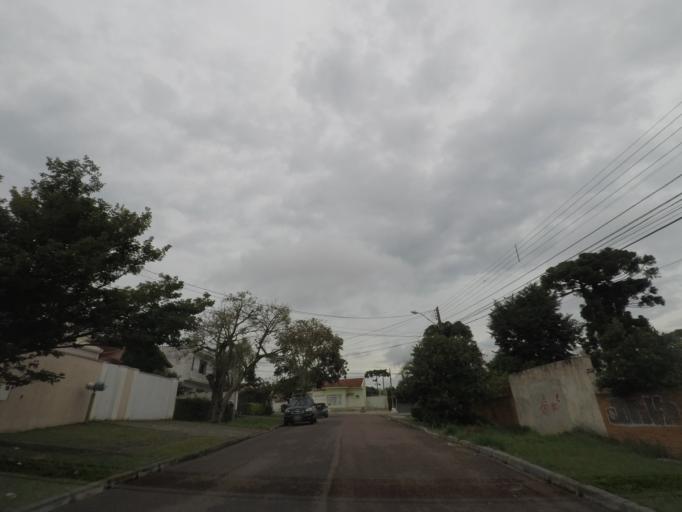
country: BR
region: Parana
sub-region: Curitiba
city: Curitiba
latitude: -25.4675
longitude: -49.3015
